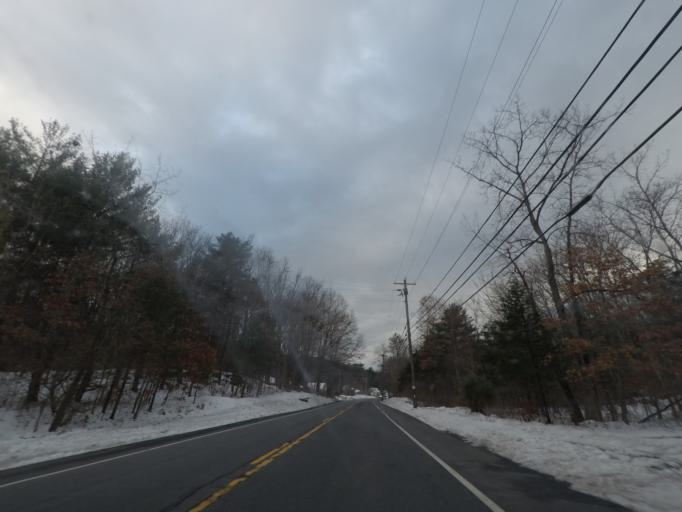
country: US
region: New York
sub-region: Ulster County
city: Hurley
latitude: 41.9014
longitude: -74.0288
